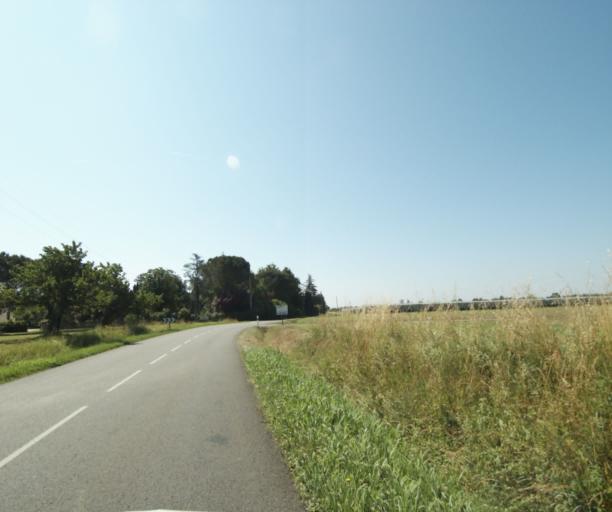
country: FR
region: Midi-Pyrenees
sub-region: Departement du Tarn-et-Garonne
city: Montbeton
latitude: 44.0490
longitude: 1.2917
